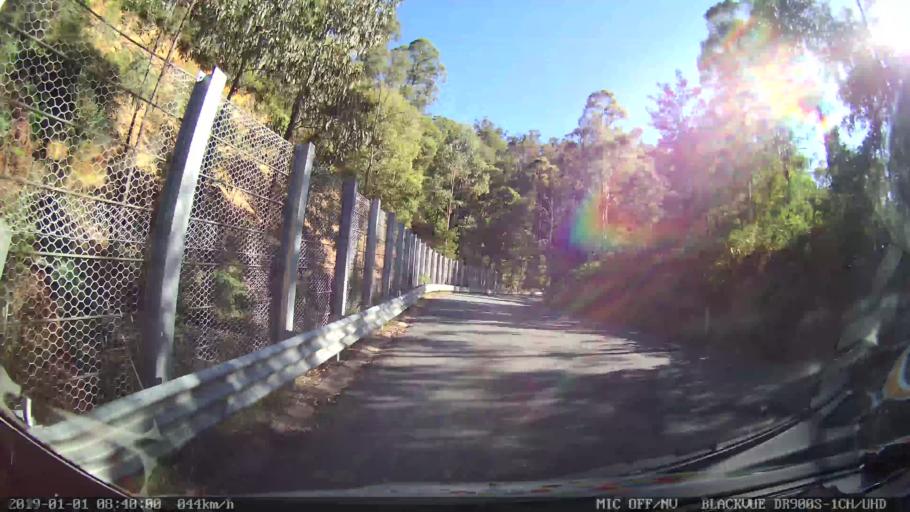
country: AU
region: New South Wales
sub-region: Snowy River
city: Jindabyne
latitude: -36.3276
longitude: 148.1943
